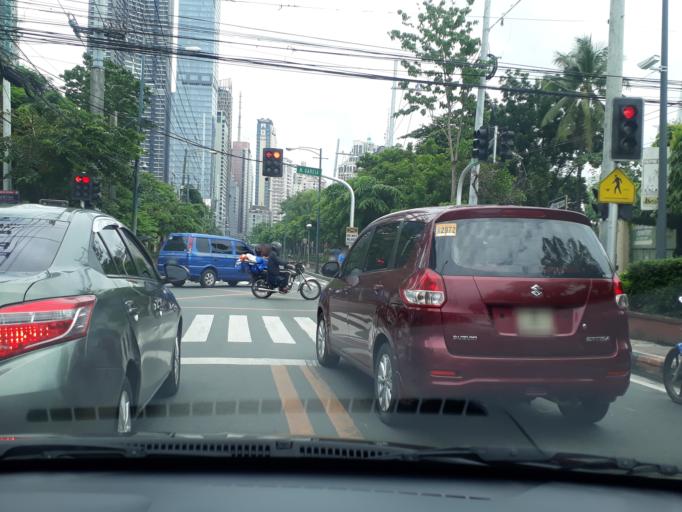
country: PH
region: Metro Manila
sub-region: Makati City
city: Makati City
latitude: 14.5668
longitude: 121.0233
